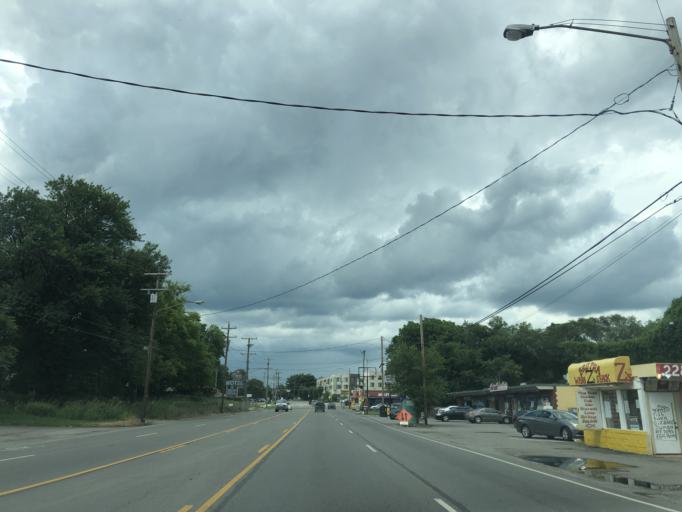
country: US
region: Tennessee
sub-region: Davidson County
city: Nashville
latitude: 36.1980
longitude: -86.7710
